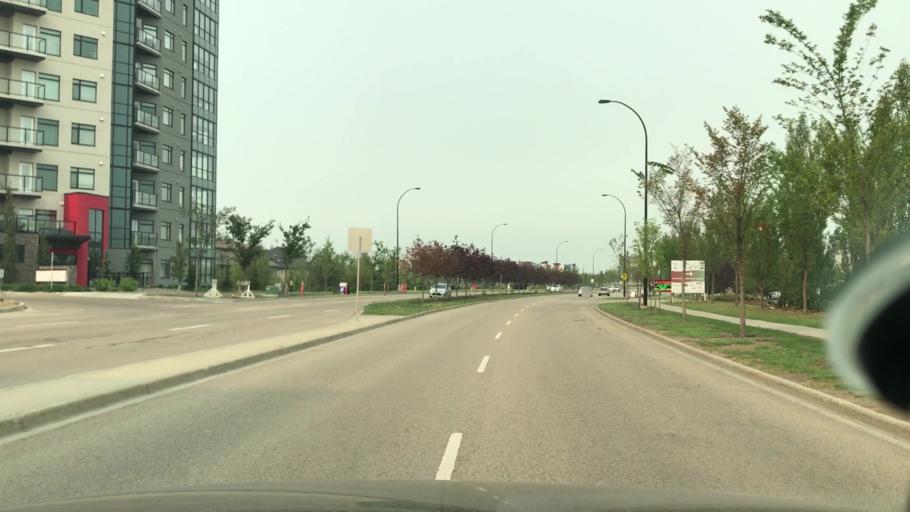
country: CA
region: Alberta
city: Devon
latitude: 53.4344
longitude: -113.6002
